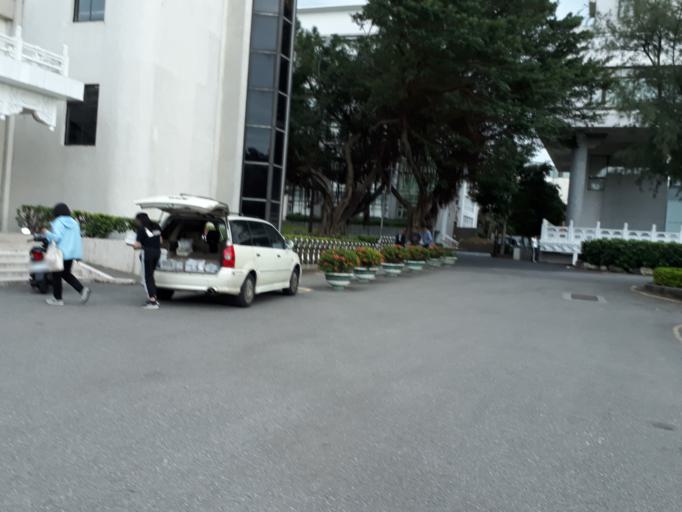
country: TW
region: Taipei
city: Taipei
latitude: 25.1754
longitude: 121.4509
